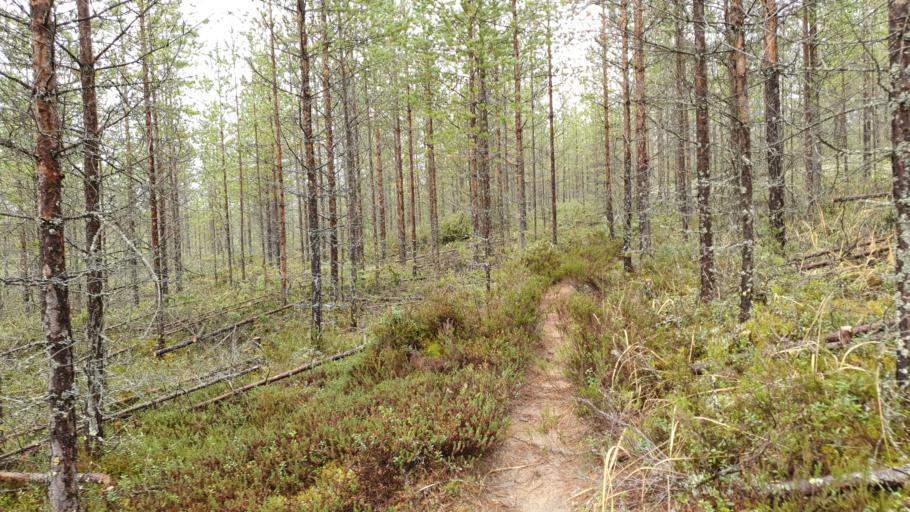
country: FI
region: Kainuu
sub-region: Kehys-Kainuu
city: Kuhmo
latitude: 64.1490
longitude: 29.4012
